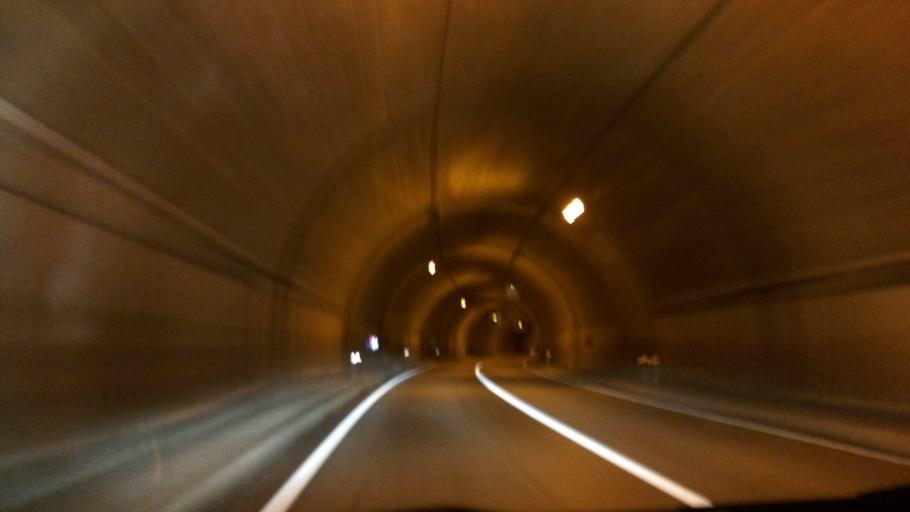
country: JP
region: Fukushima
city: Kitakata
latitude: 37.3615
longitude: 139.8776
